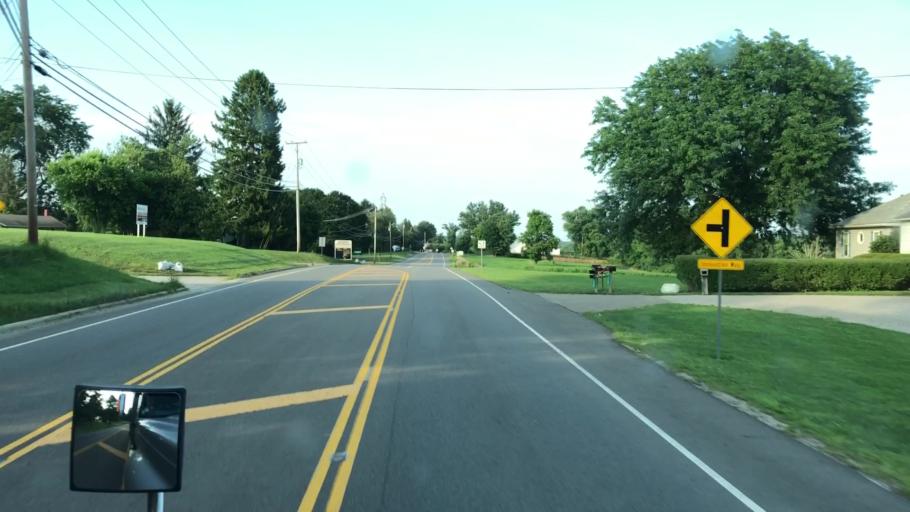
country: US
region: Ohio
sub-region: Muskingum County
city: Pleasant Grove
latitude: 39.9734
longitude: -81.9507
